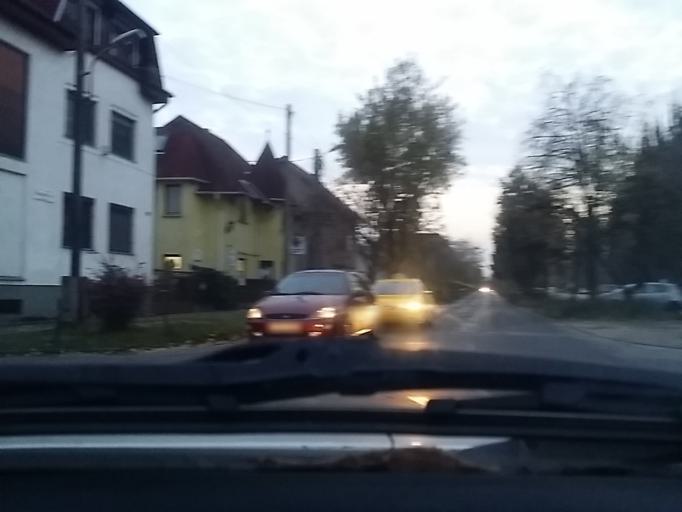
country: HU
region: Budapest
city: Budapest XIV. keruelet
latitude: 47.5202
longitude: 19.1349
